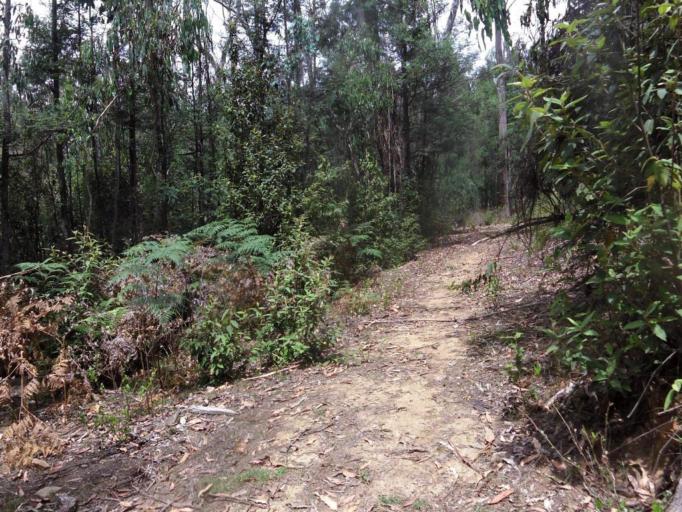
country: AU
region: Victoria
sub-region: Yarra Ranges
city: Healesville
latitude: -37.4397
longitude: 145.5787
